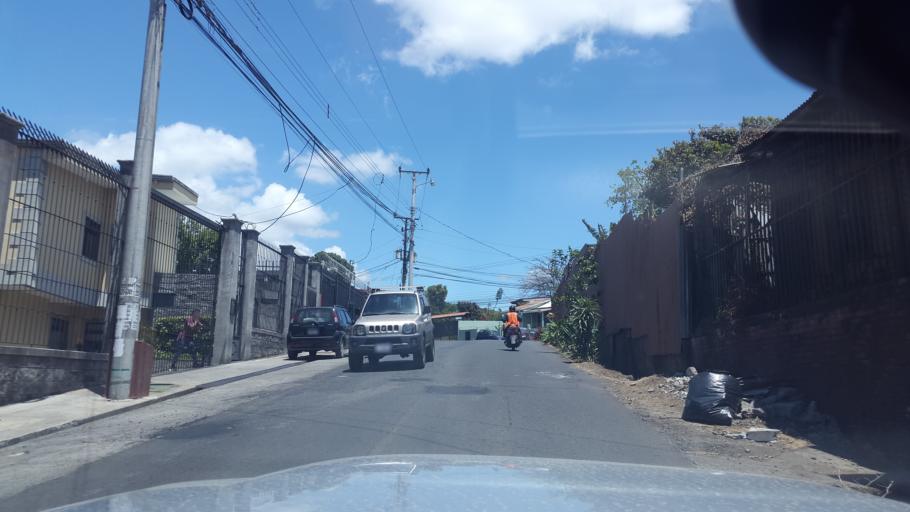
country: CR
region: San Jose
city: San Pedro
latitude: 9.9348
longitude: -84.0422
